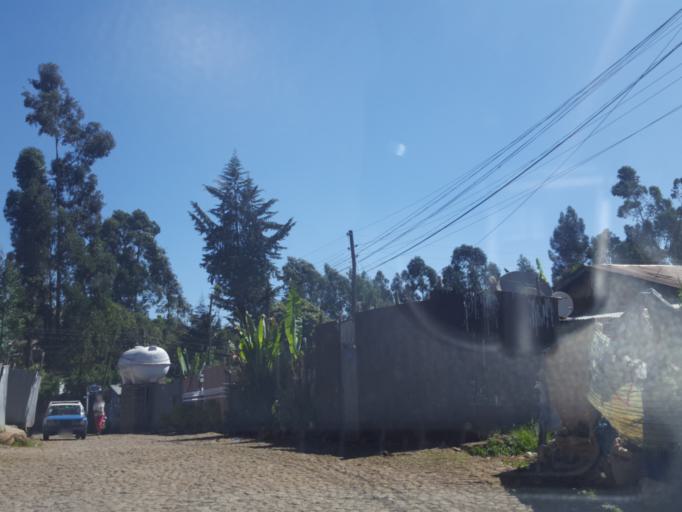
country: ET
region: Adis Abeba
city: Addis Ababa
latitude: 9.0549
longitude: 38.7464
